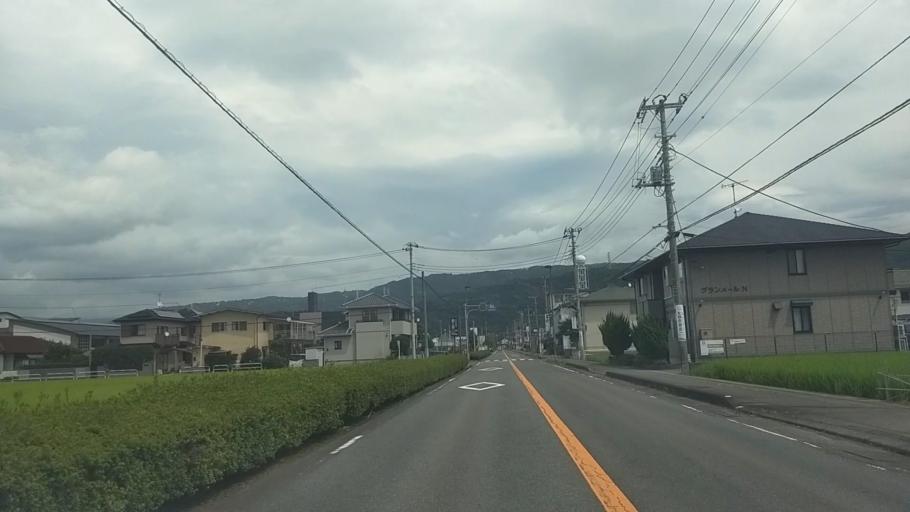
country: JP
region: Shizuoka
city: Mishima
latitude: 35.0585
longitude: 138.9503
